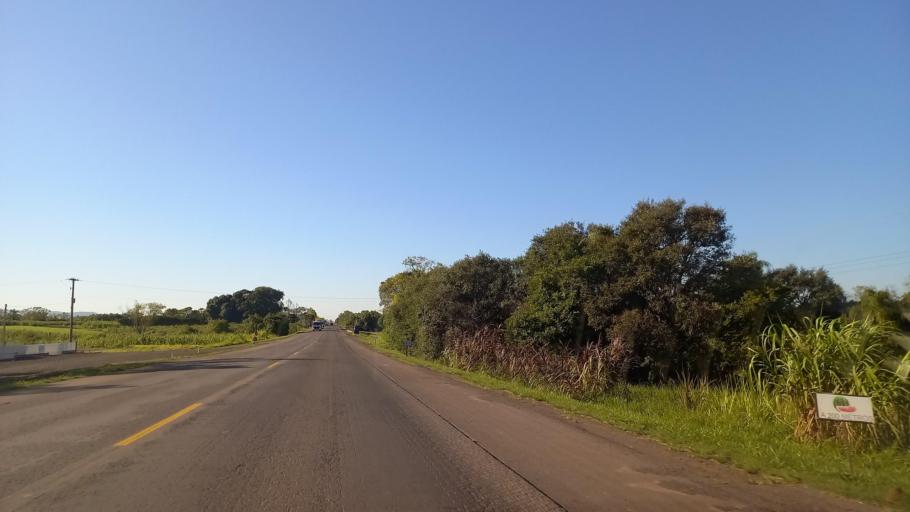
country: BR
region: Rio Grande do Sul
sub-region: Venancio Aires
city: Venancio Aires
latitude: -29.6702
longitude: -52.0247
